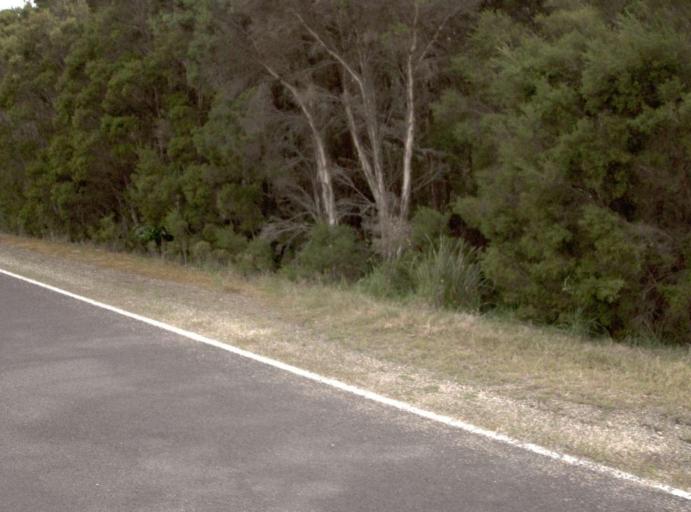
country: AU
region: New South Wales
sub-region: Bombala
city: Bombala
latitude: -37.4348
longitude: 149.1997
